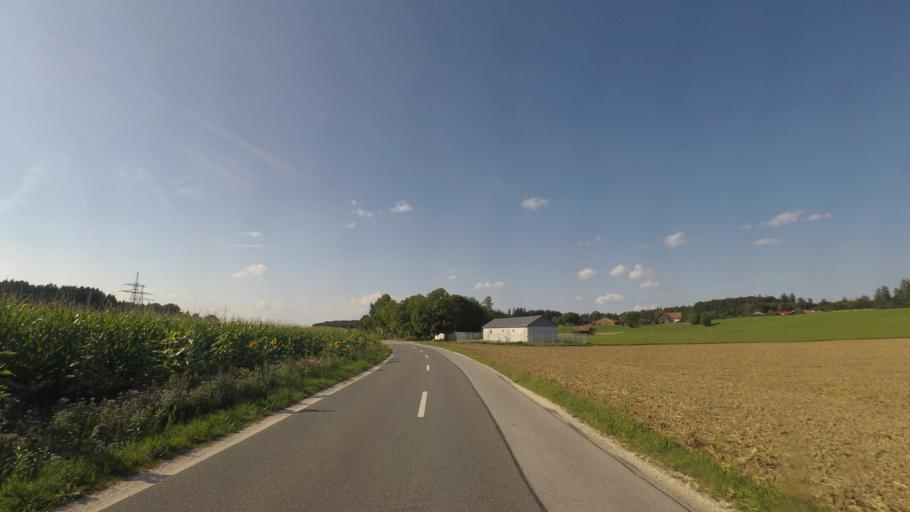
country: DE
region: Bavaria
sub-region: Upper Bavaria
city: Traunstein
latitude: 47.8806
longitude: 12.6195
